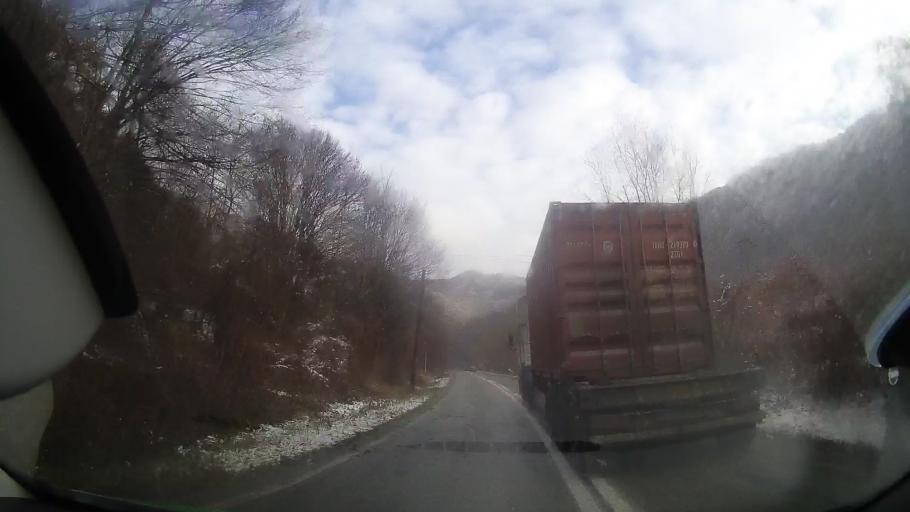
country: RO
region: Alba
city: Salciua de Sus
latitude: 46.4022
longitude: 23.3506
